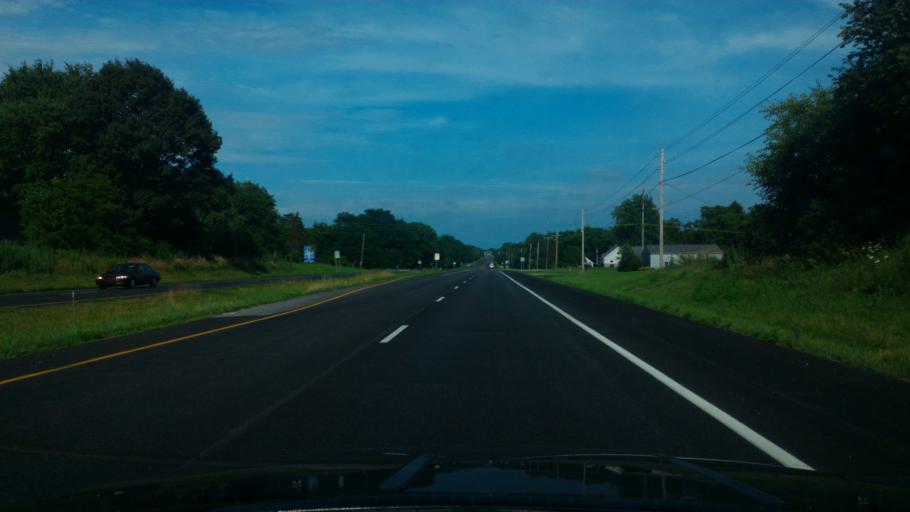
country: US
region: Indiana
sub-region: Tippecanoe County
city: West Lafayette
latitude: 40.4673
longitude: -86.9830
